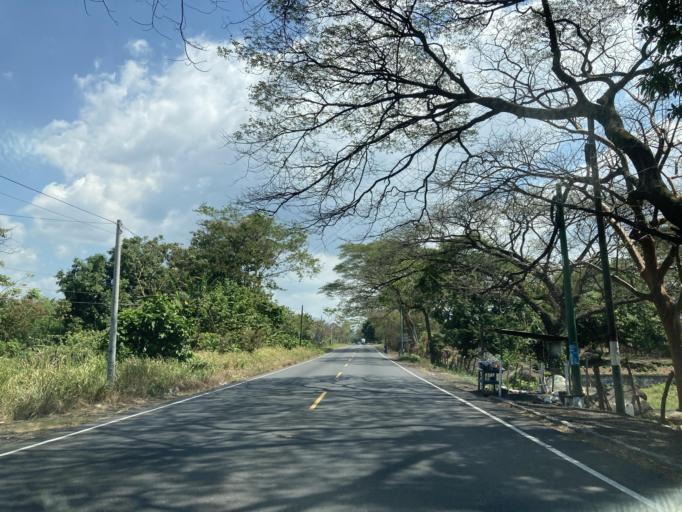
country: GT
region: Santa Rosa
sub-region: Municipio de Taxisco
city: Taxisco
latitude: 14.0934
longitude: -90.5537
